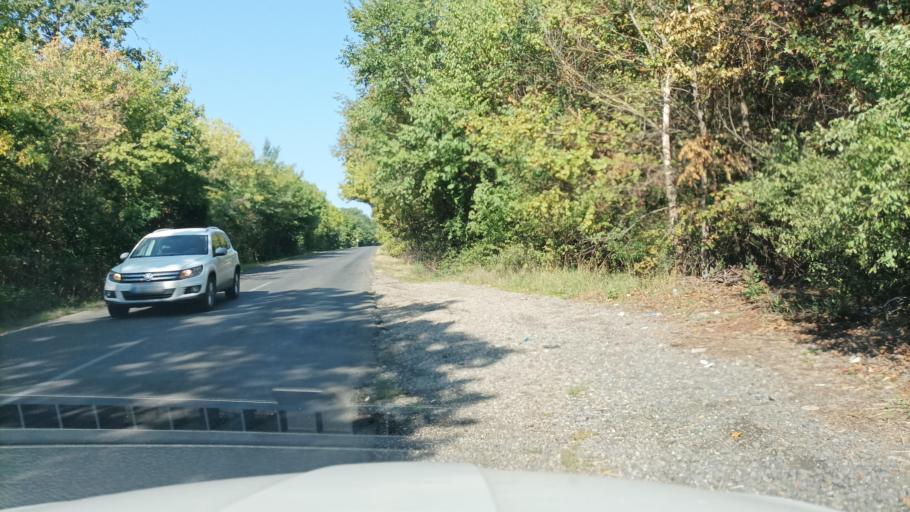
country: HU
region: Pest
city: Valko
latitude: 47.5648
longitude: 19.4560
